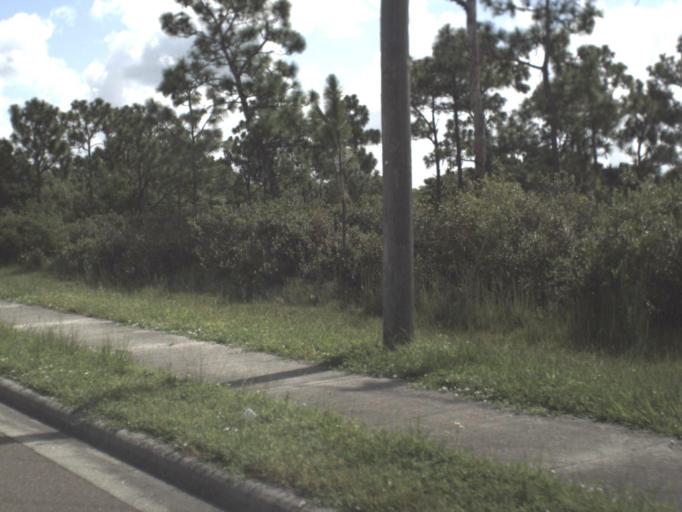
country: US
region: Florida
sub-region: Charlotte County
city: Cleveland
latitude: 26.9504
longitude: -81.9984
